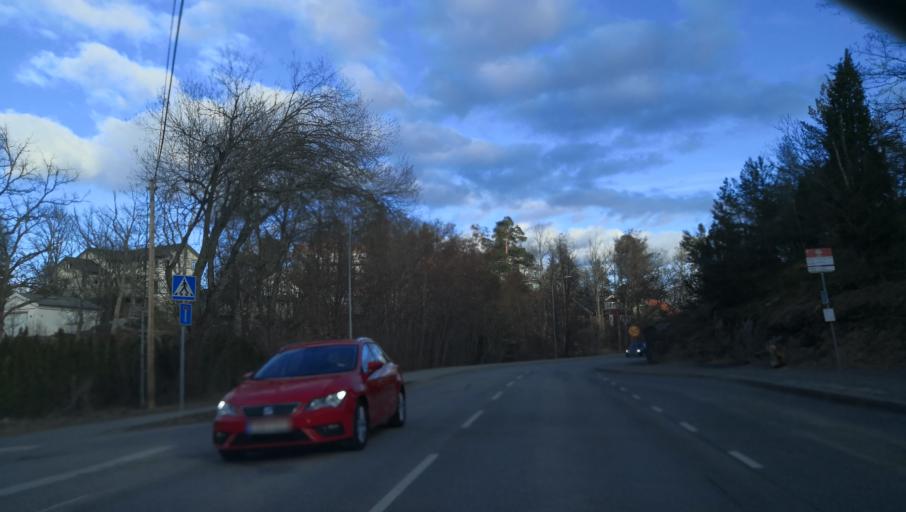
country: SE
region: Stockholm
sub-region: Nacka Kommun
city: Boo
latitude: 59.3335
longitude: 18.3360
